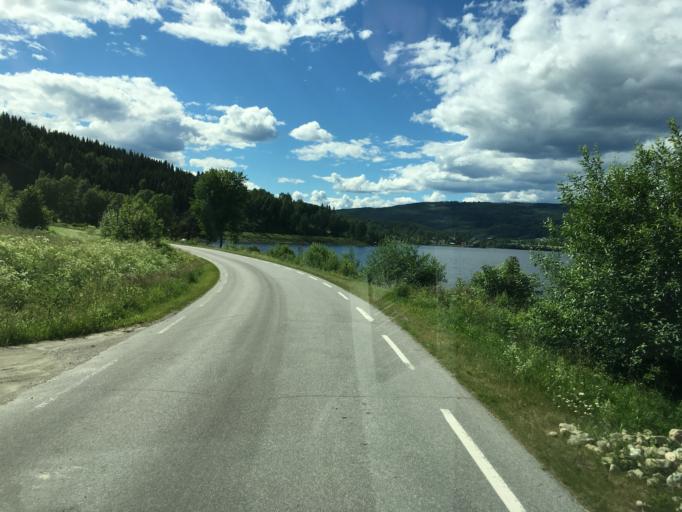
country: NO
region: Oppland
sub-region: Sondre Land
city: Hov
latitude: 60.5118
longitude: 10.3261
